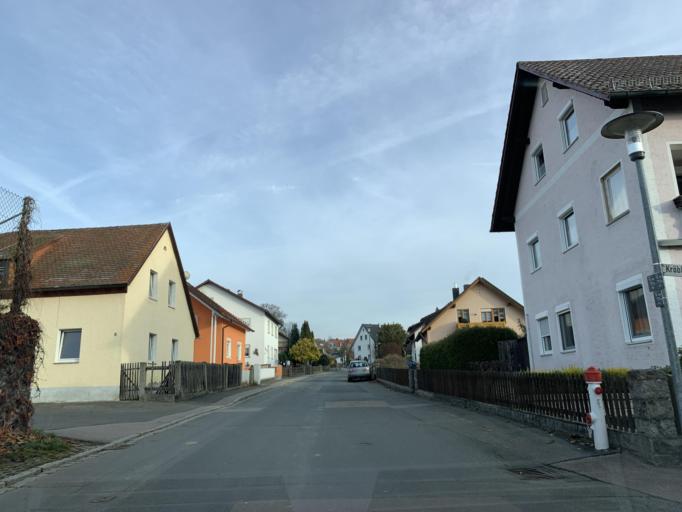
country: DE
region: Bavaria
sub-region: Upper Palatinate
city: Neunburg vorm Wald
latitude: 49.3529
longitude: 12.3840
